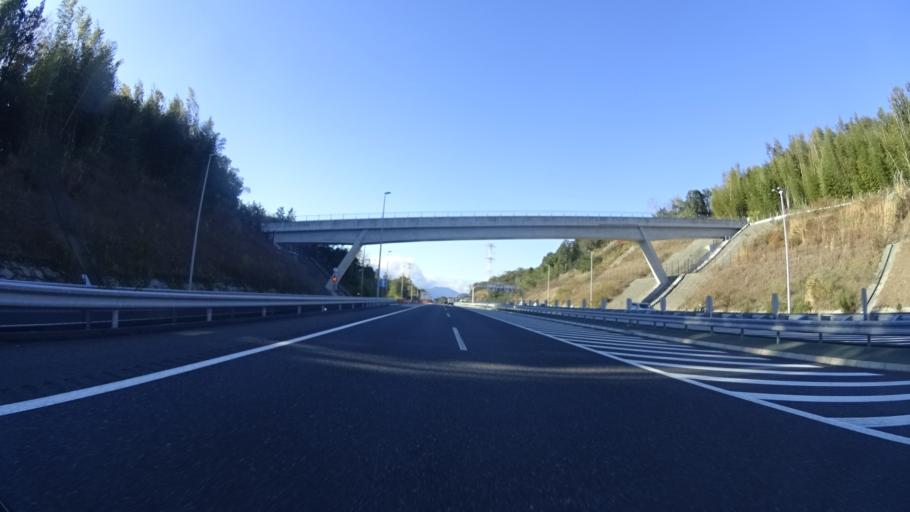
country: JP
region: Mie
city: Yokkaichi
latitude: 35.0406
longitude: 136.6237
